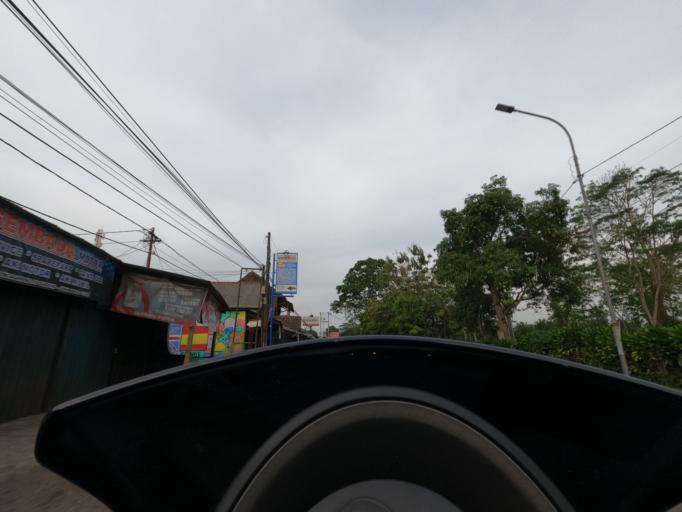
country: ID
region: West Java
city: Lembang
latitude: -6.6778
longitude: 107.6901
